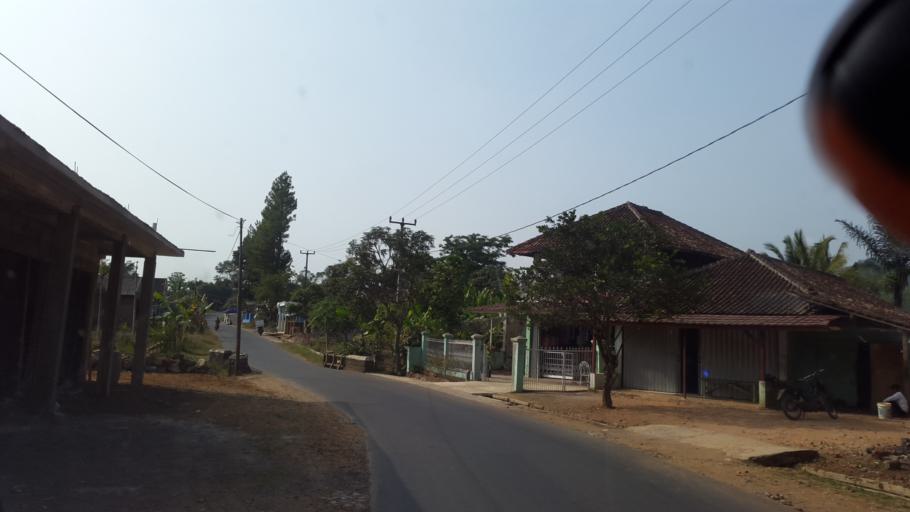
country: ID
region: West Java
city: Citampian
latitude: -7.1585
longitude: 106.7618
